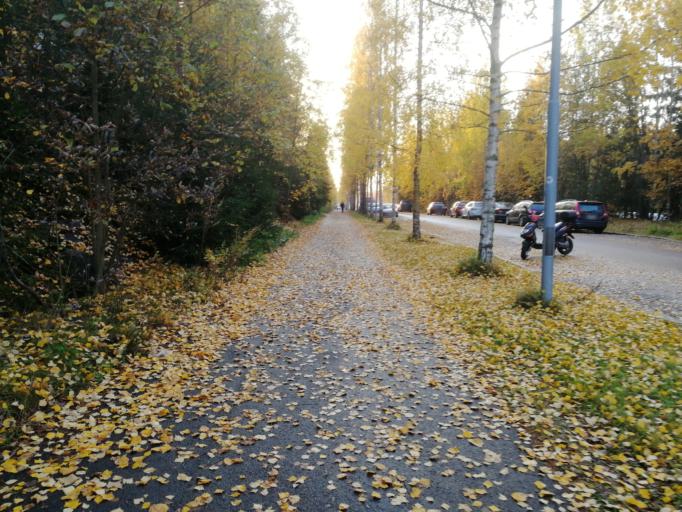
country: FI
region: Pirkanmaa
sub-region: Tampere
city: Tampere
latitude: 61.4523
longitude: 23.8603
